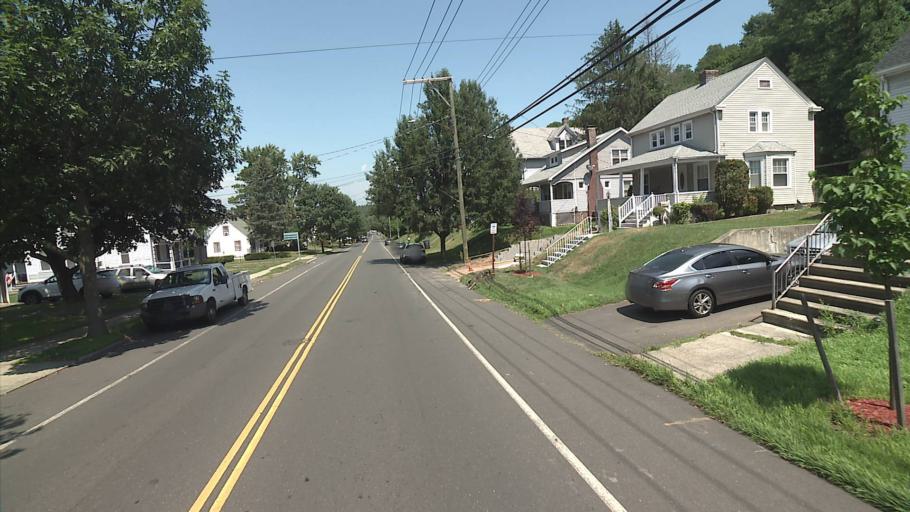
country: US
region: Connecticut
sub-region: New Haven County
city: East Haven
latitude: 41.2843
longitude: -72.8936
